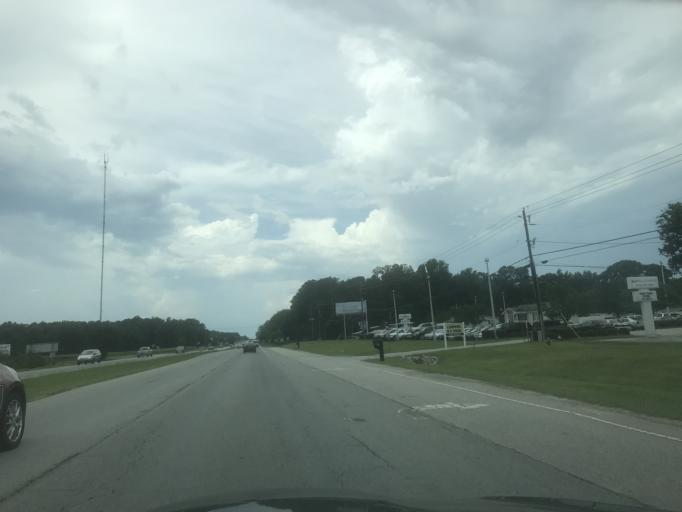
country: US
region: North Carolina
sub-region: Johnston County
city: Clayton
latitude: 35.6705
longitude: -78.5083
